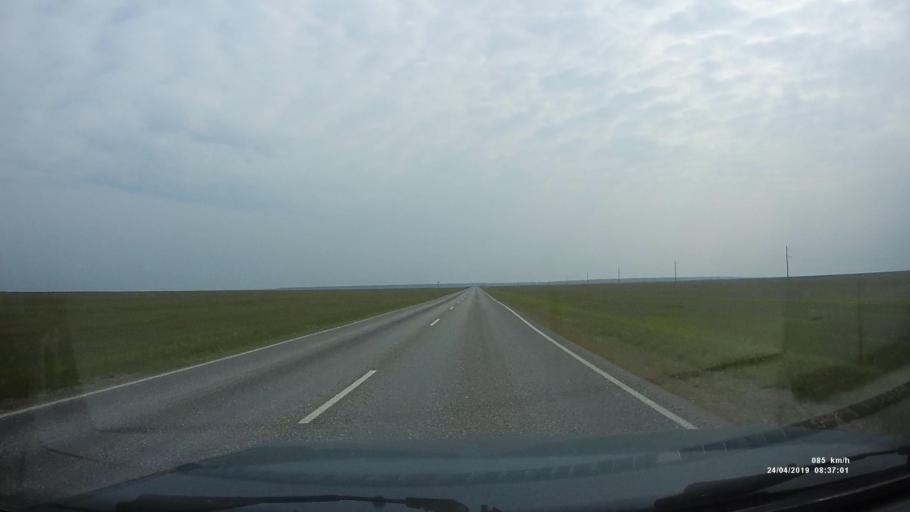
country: RU
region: Kalmykiya
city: Arshan'
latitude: 46.2078
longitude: 43.9440
